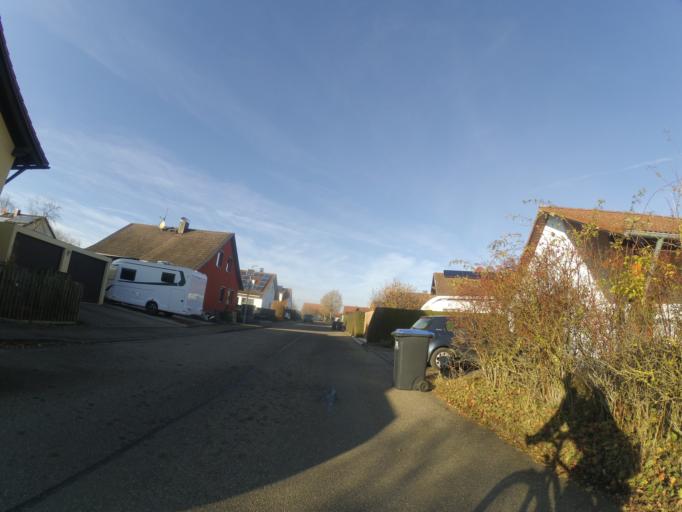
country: DE
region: Baden-Wuerttemberg
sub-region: Tuebingen Region
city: Dornstadt
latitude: 48.4579
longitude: 9.9131
